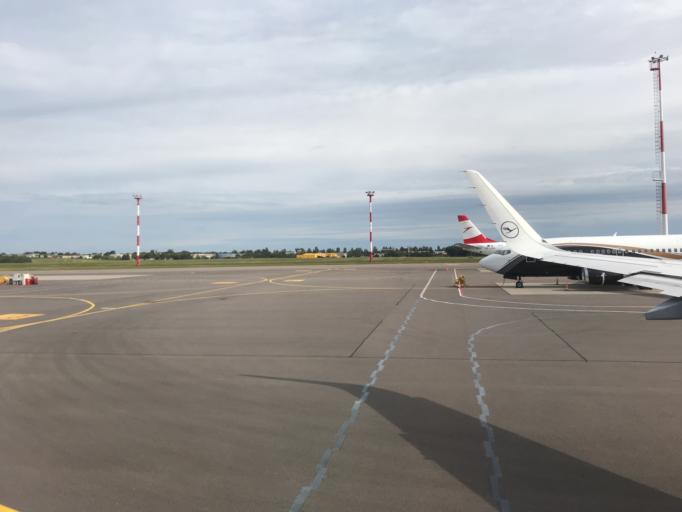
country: LT
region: Vilnius County
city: Naujamiestis
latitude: 54.6438
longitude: 25.2838
